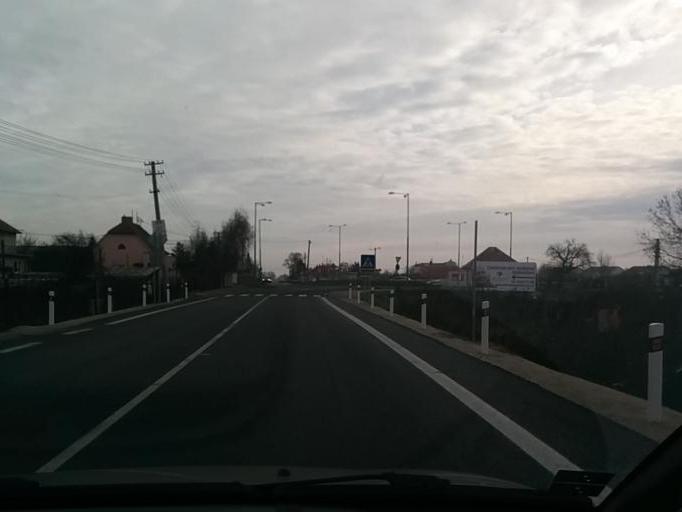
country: SK
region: Trnavsky
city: Sladkovicovo
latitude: 48.2083
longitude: 17.6489
